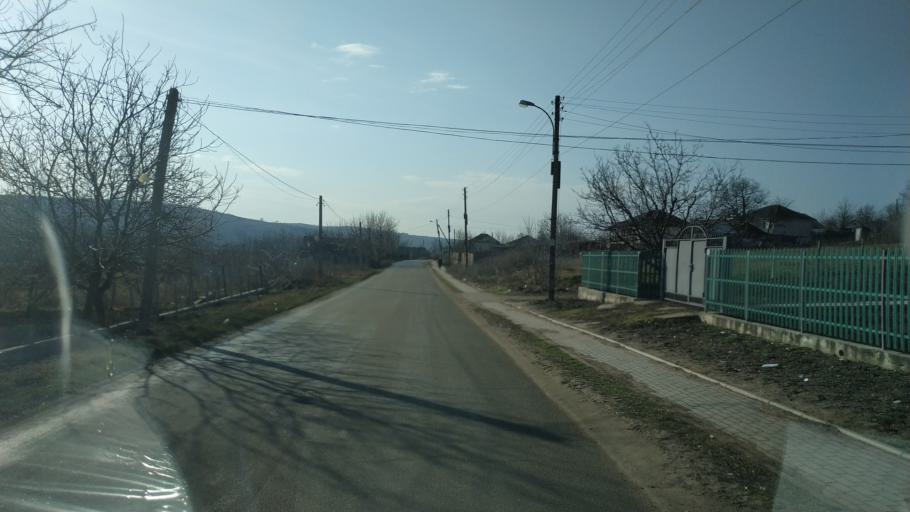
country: MD
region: Chisinau
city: Singera
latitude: 46.8213
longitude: 29.0375
